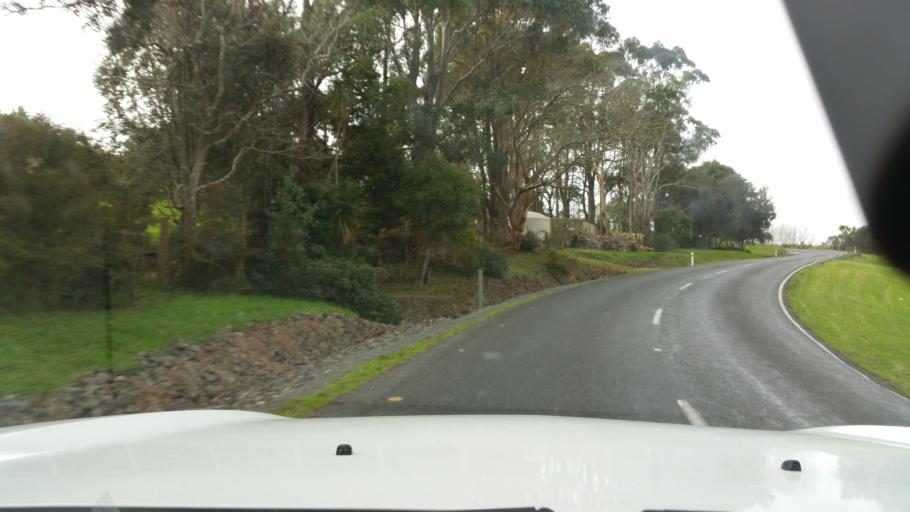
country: NZ
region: Northland
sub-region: Whangarei
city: Ngunguru
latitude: -35.7628
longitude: 174.4962
